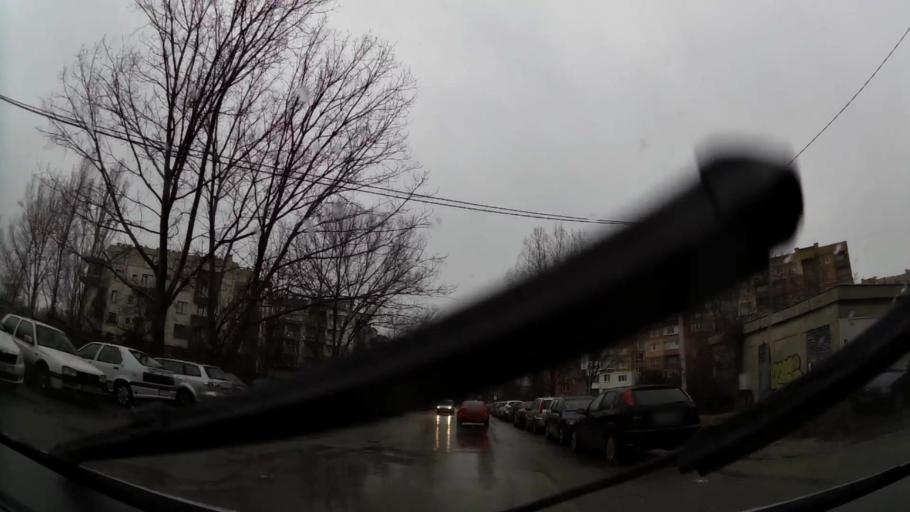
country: BG
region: Sofia-Capital
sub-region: Stolichna Obshtina
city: Sofia
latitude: 42.6653
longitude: 23.3795
